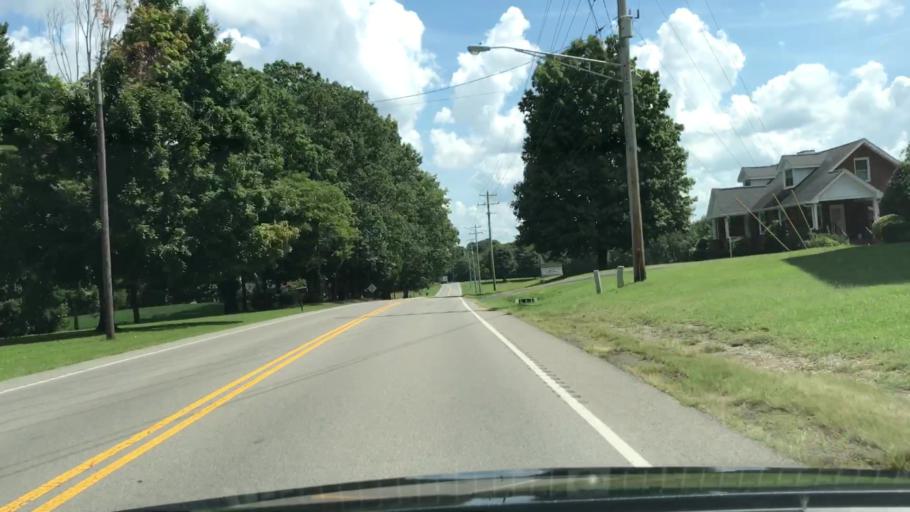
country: US
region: Tennessee
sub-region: Robertson County
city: Cross Plains
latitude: 36.5516
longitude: -86.7378
